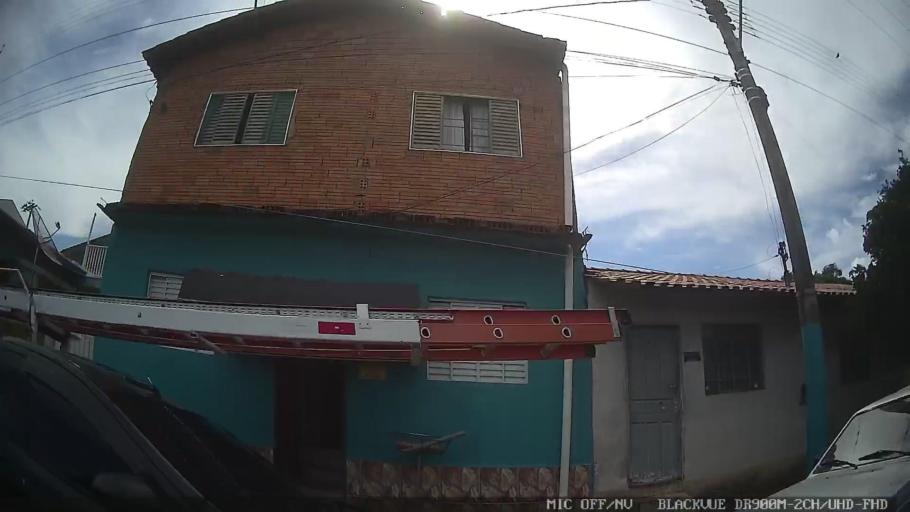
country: BR
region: Sao Paulo
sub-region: Conchas
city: Conchas
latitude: -23.0139
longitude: -48.0035
